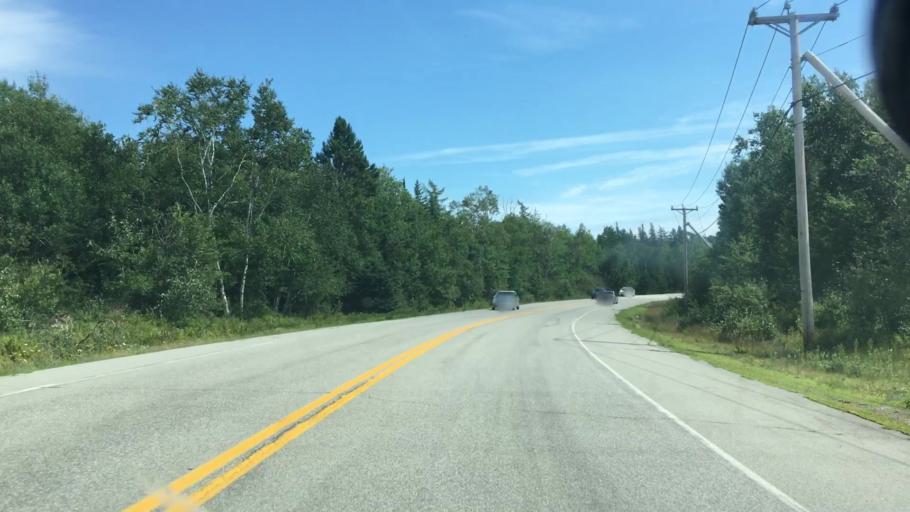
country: US
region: Maine
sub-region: Washington County
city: Eastport
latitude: 44.9378
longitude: -67.0286
